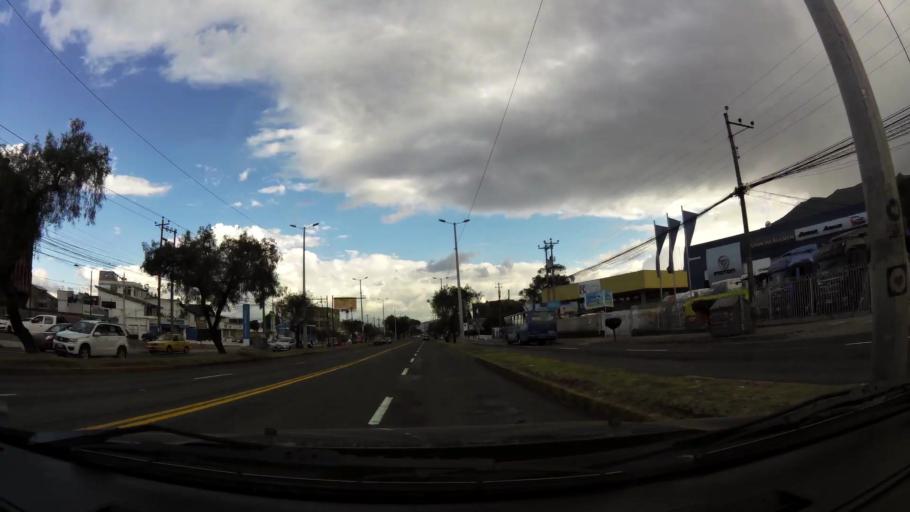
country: EC
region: Pichincha
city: Quito
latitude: -0.1422
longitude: -78.4831
